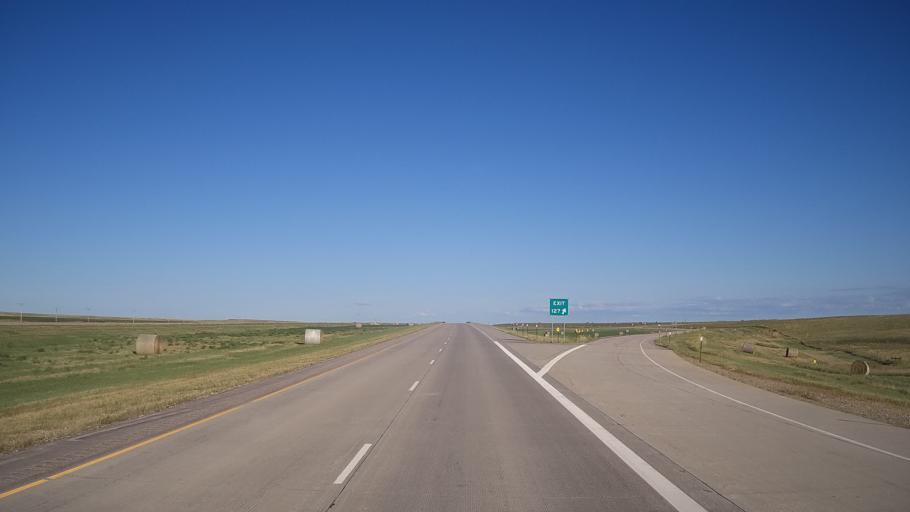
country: US
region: South Dakota
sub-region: Haakon County
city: Philip
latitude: 43.8694
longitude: -101.9650
